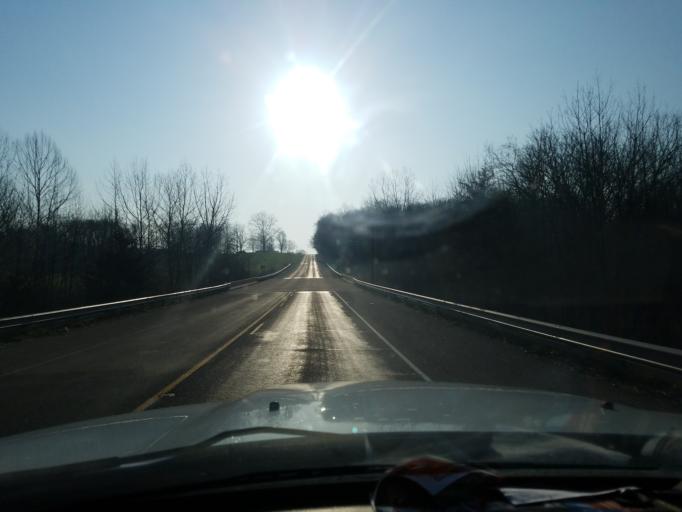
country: US
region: Indiana
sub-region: Clay County
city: Middlebury
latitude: 39.3880
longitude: -87.1686
